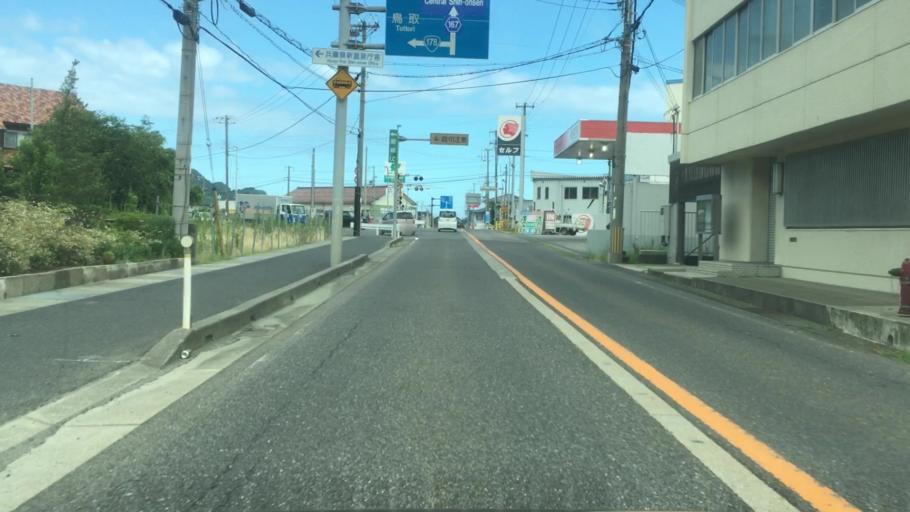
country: JP
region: Tottori
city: Tottori
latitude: 35.6186
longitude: 134.4623
